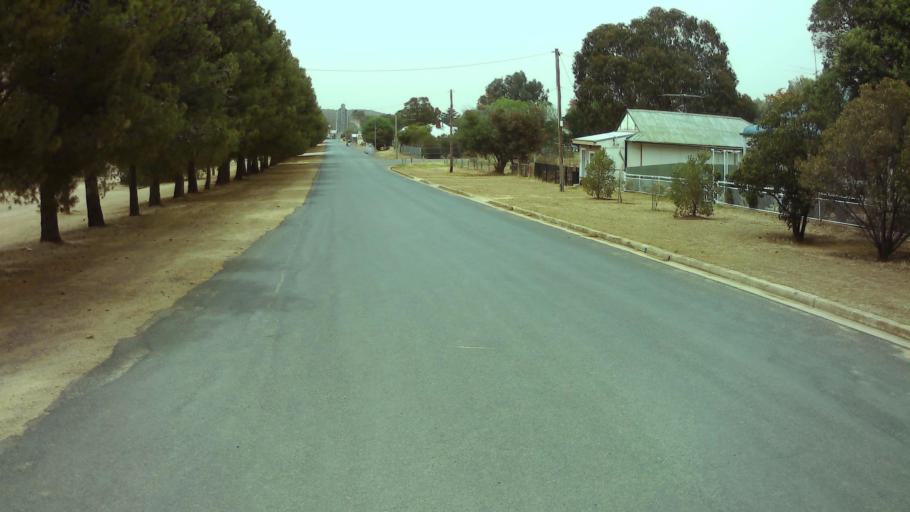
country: AU
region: New South Wales
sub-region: Weddin
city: Grenfell
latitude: -33.9001
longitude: 148.1552
